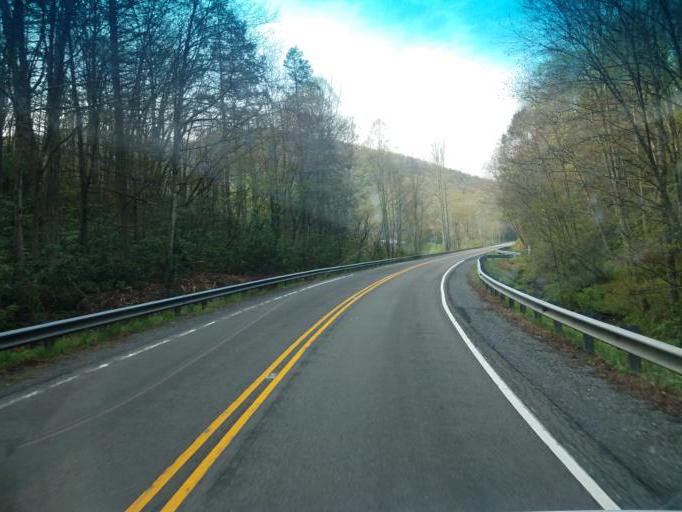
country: US
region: Virginia
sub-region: Smyth County
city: Atkins
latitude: 36.8093
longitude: -81.4041
